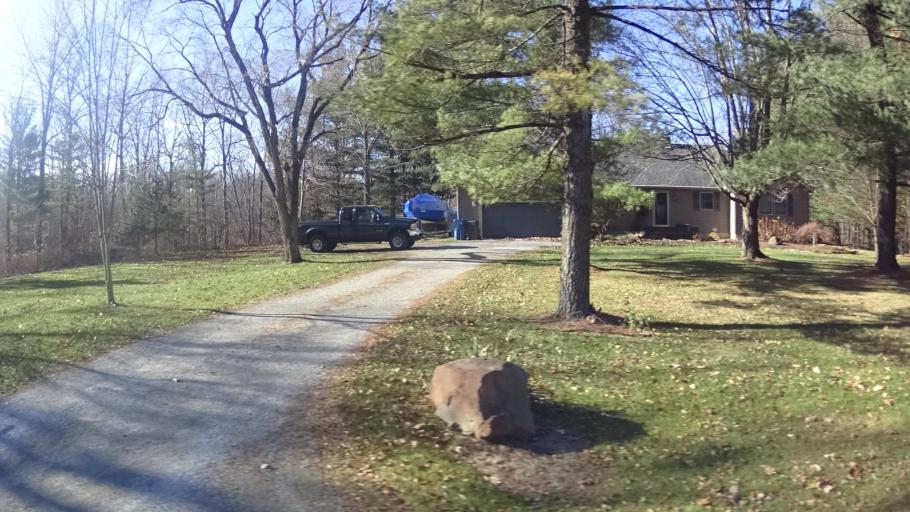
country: US
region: Ohio
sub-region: Lorain County
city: South Amherst
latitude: 41.3519
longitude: -82.2912
